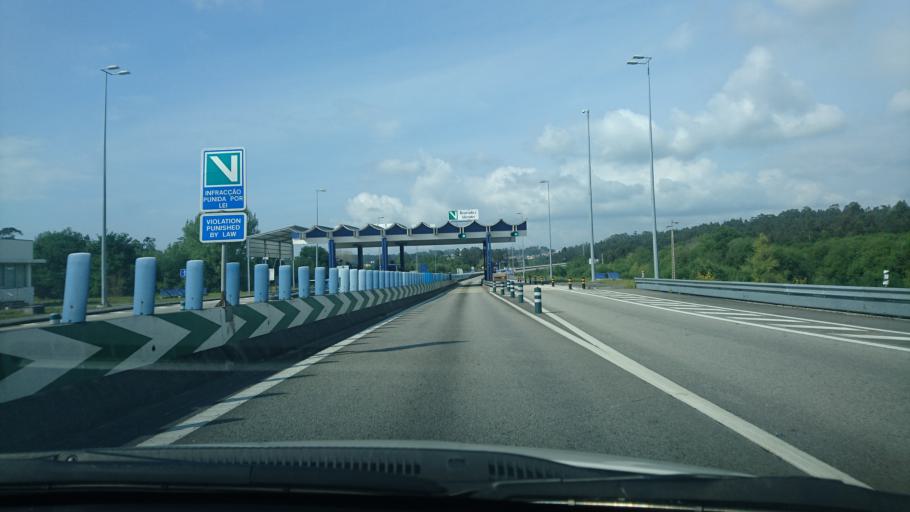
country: PT
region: Aveiro
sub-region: Santa Maria da Feira
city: Argoncilhe
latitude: 41.0140
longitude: -8.5294
